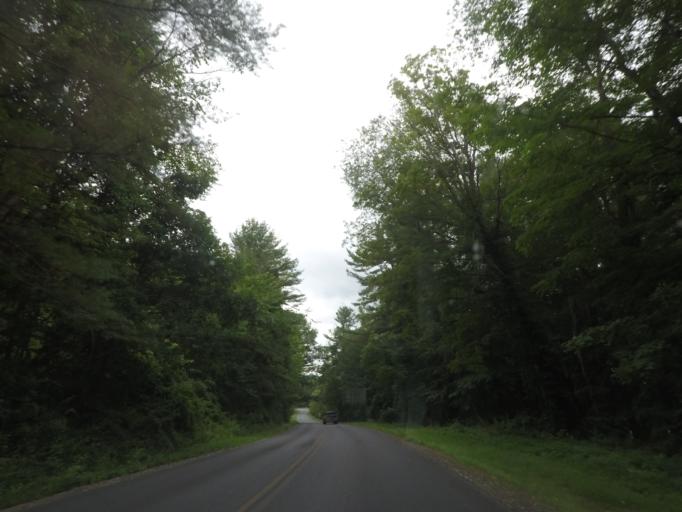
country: US
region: New York
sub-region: Saratoga County
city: Stillwater
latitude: 42.8561
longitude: -73.5499
